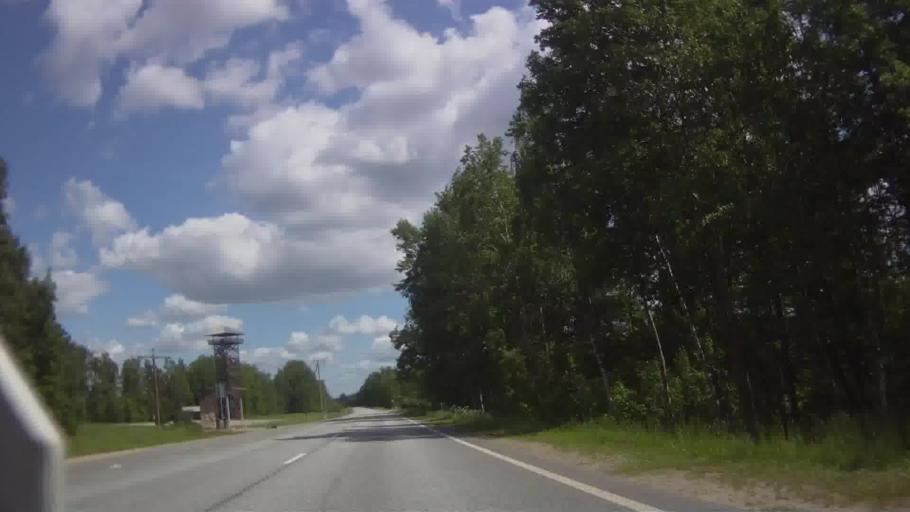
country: LV
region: Varaklani
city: Varaklani
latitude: 56.5388
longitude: 26.5643
